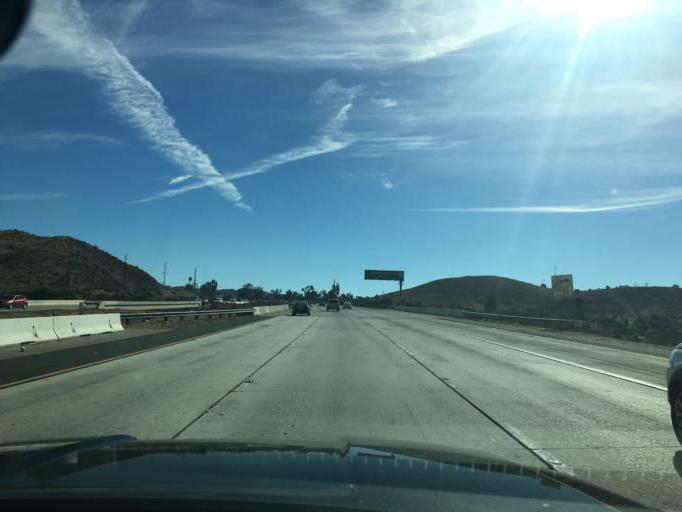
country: US
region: California
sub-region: Riverside County
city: Lake Elsinore
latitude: 33.6778
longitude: -117.3246
